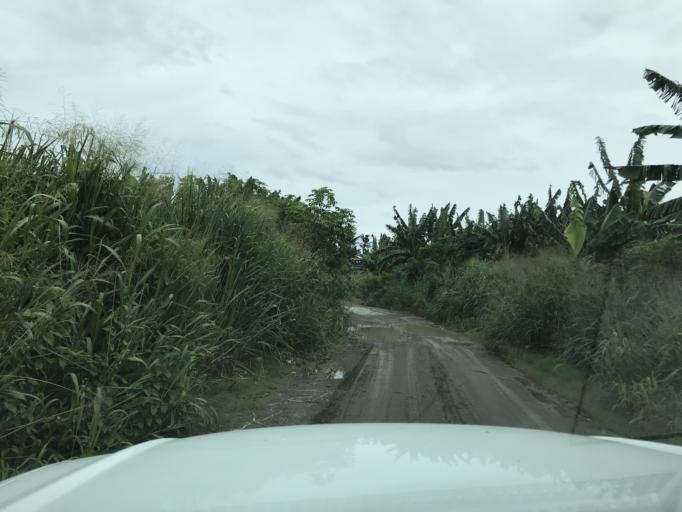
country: SB
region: Guadalcanal
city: Honiara
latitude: -9.4345
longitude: 160.0349
